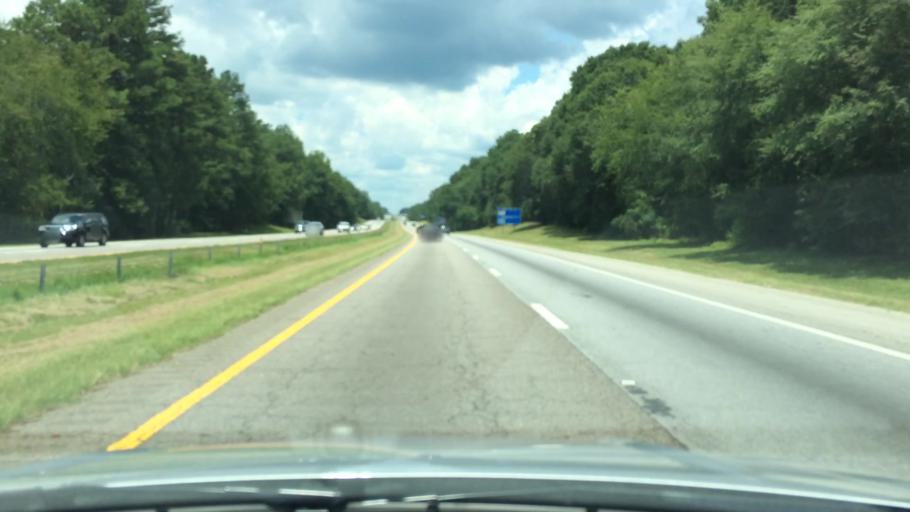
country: US
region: South Carolina
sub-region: Newberry County
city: Newberry
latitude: 34.3020
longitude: -81.5586
